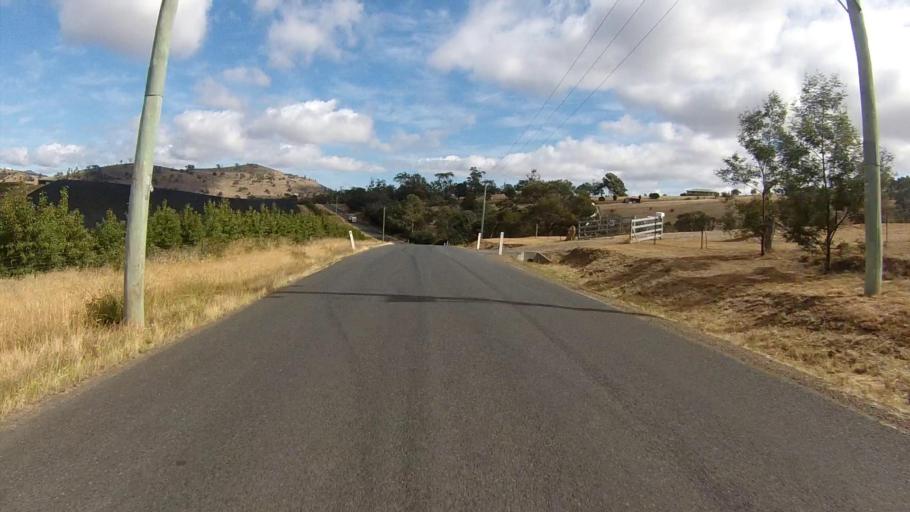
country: AU
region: Tasmania
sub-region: Brighton
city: Old Beach
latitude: -42.7412
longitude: 147.3015
